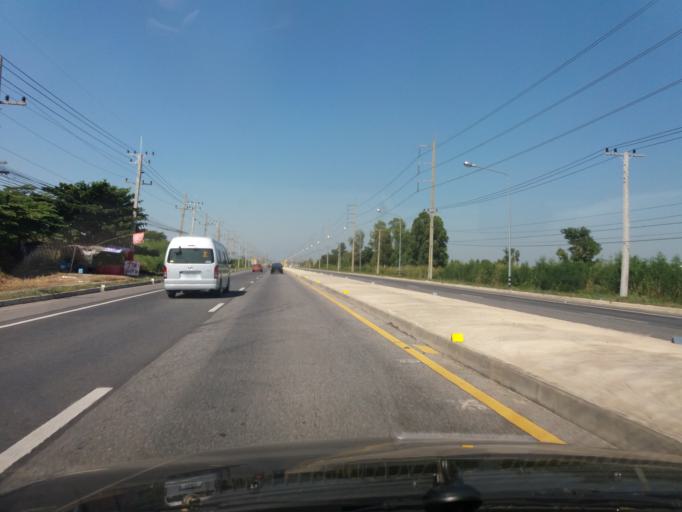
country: TH
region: Chai Nat
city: Manorom
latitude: 15.2917
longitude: 100.0983
